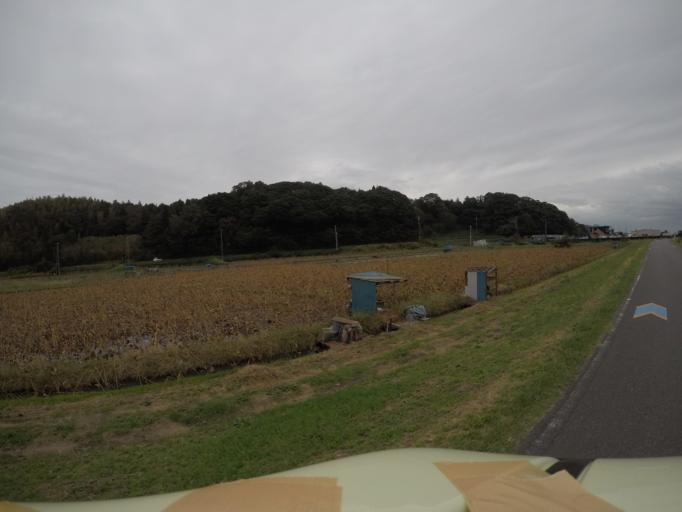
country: JP
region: Ibaraki
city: Ami
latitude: 36.0633
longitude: 140.2880
